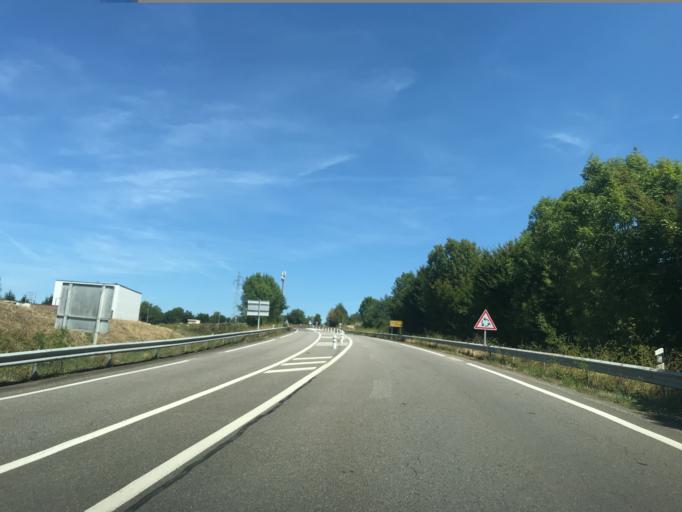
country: FR
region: Limousin
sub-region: Departement de la Correze
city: Tulle
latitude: 45.2817
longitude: 1.7971
